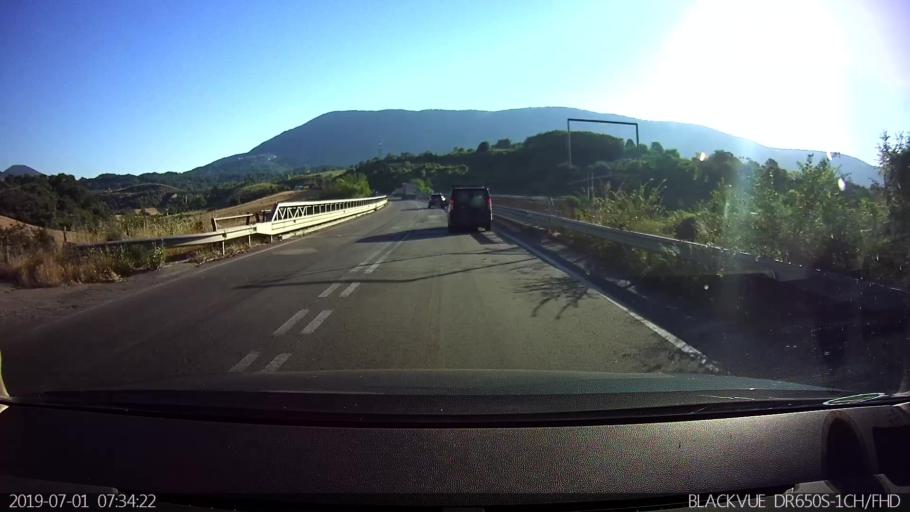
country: IT
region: Latium
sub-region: Provincia di Latina
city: Prossedi
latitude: 41.5152
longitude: 13.2711
